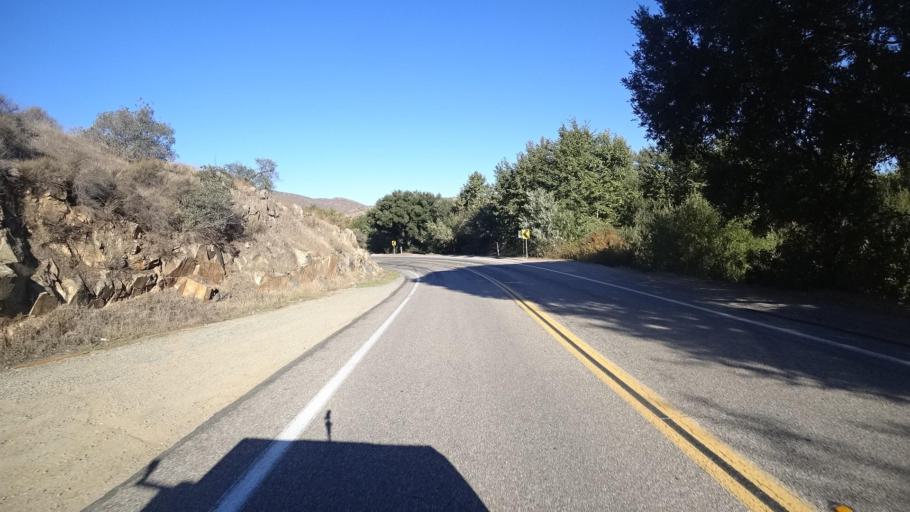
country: US
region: California
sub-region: San Diego County
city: Jamul
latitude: 32.6505
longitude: -116.8650
